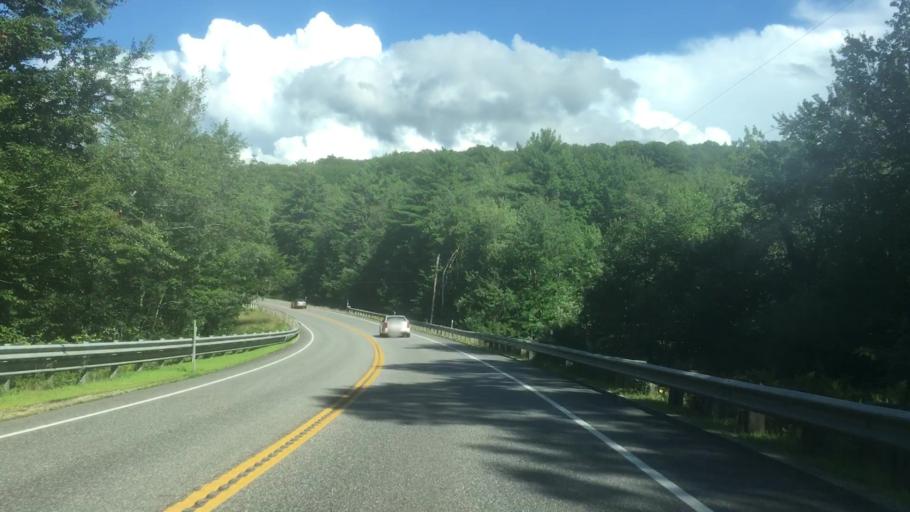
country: US
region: New Hampshire
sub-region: Hillsborough County
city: Antrim
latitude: 43.0672
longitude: -72.0298
